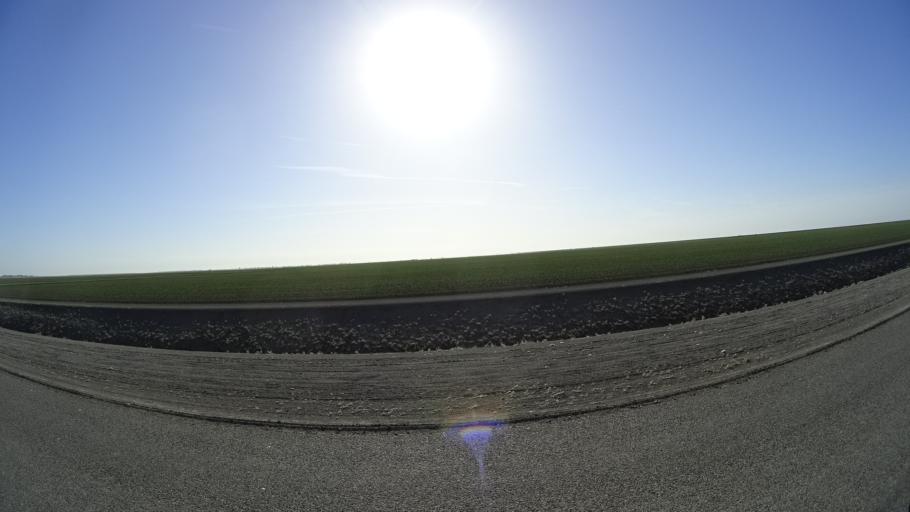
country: US
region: California
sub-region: Kings County
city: Stratford
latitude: 36.1223
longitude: -119.7981
